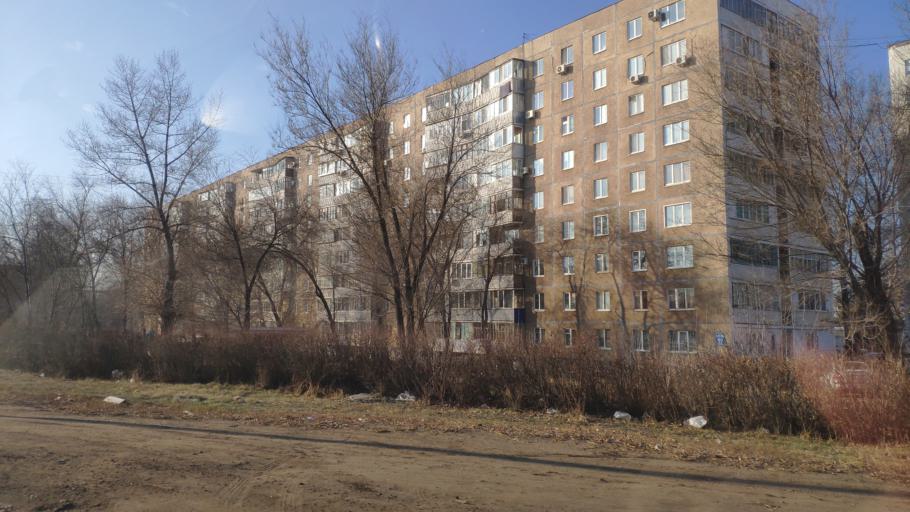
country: RU
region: Orenburg
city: Prigorodnyy
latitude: 51.7797
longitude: 55.1892
